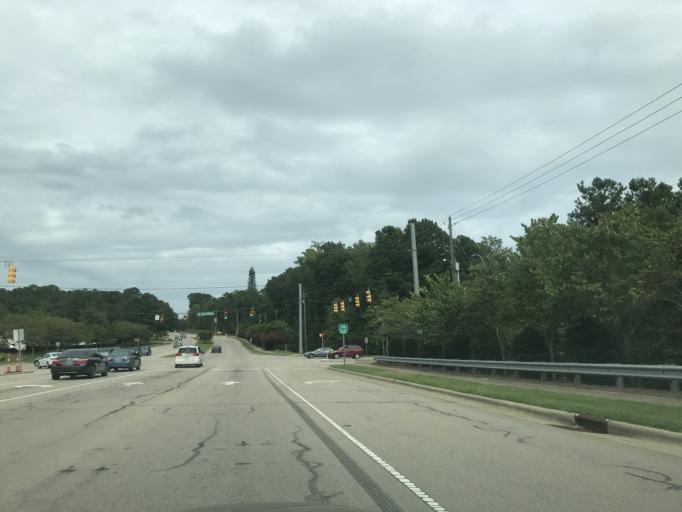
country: US
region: North Carolina
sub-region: Wake County
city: Cary
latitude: 35.7432
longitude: -78.7632
